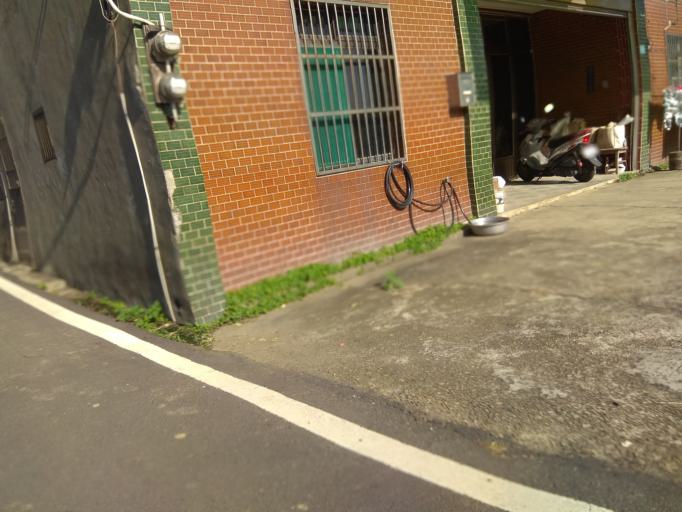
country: TW
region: Taiwan
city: Taoyuan City
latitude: 25.0625
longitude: 121.2122
